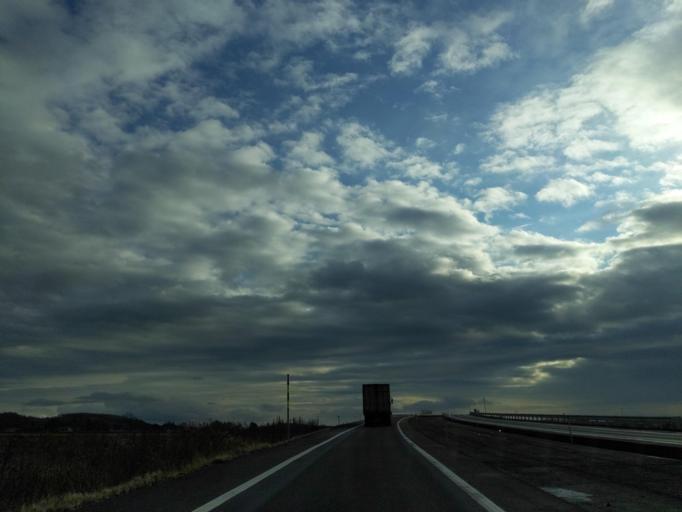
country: JP
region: Hokkaido
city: Chitose
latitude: 42.9376
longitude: 141.7145
